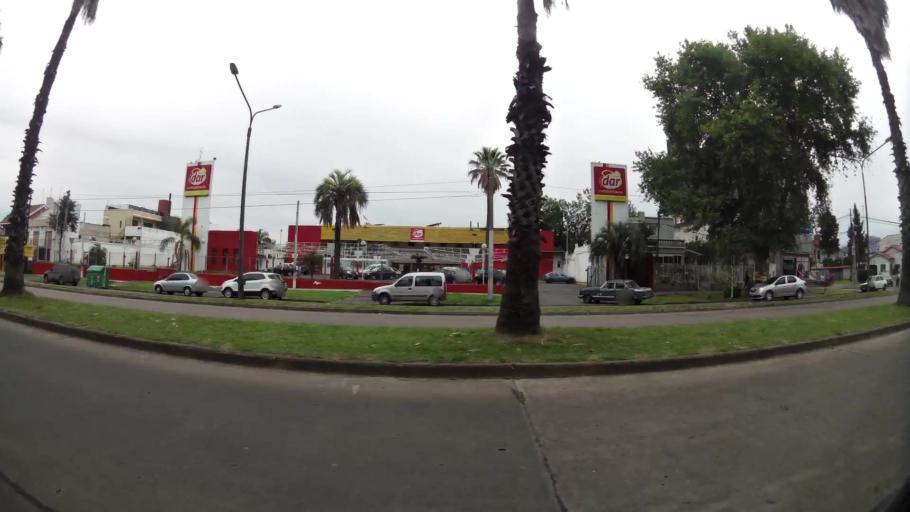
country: AR
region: Santa Fe
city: Granadero Baigorria
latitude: -32.9017
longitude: -60.6903
